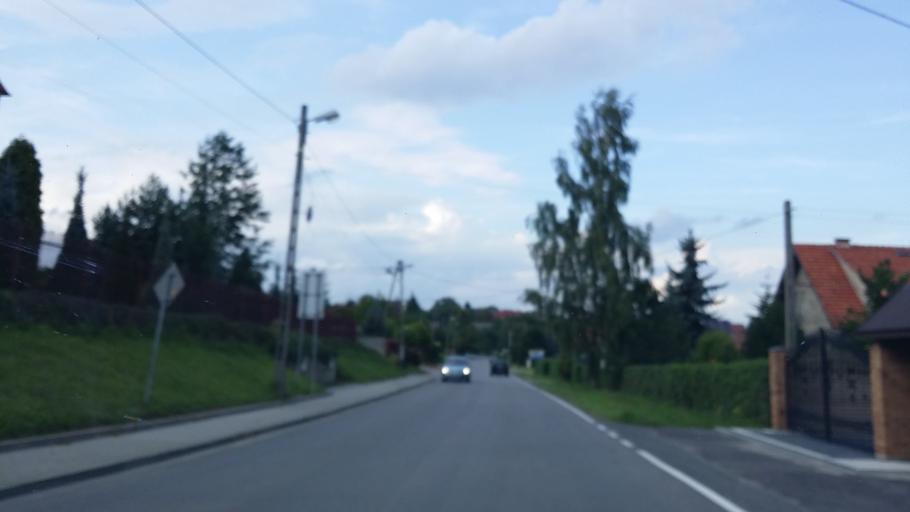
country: PL
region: Lesser Poland Voivodeship
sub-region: Powiat wielicki
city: Pawlikowice
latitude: 49.9222
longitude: 20.0287
